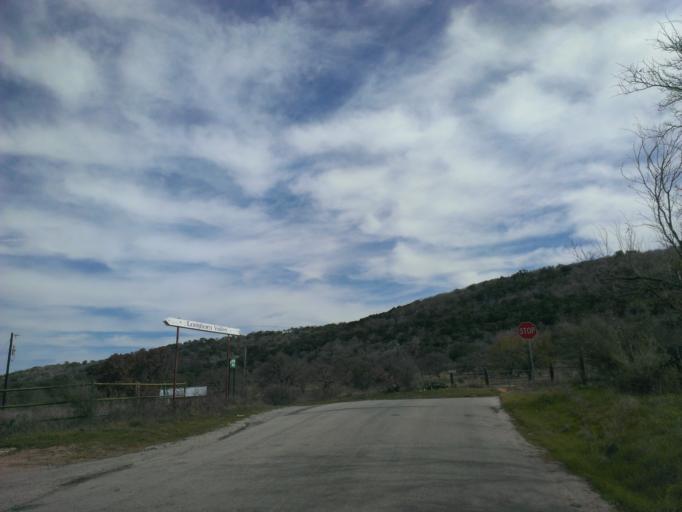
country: US
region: Texas
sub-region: Llano County
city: Kingsland
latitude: 30.6819
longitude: -98.3920
